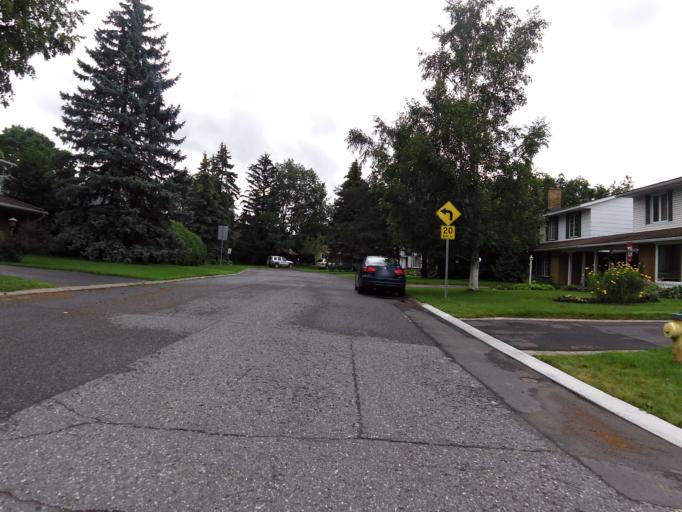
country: CA
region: Ontario
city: Bells Corners
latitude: 45.3217
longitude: -75.7812
